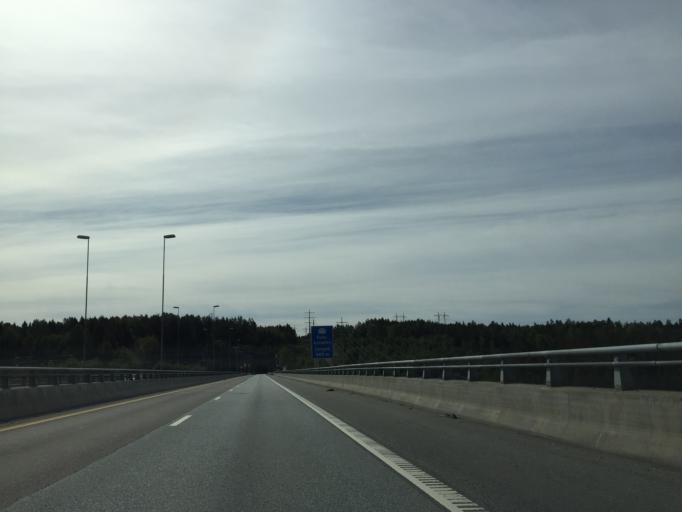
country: NO
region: Akershus
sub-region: Vestby
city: Vestby
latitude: 59.5392
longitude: 10.7263
